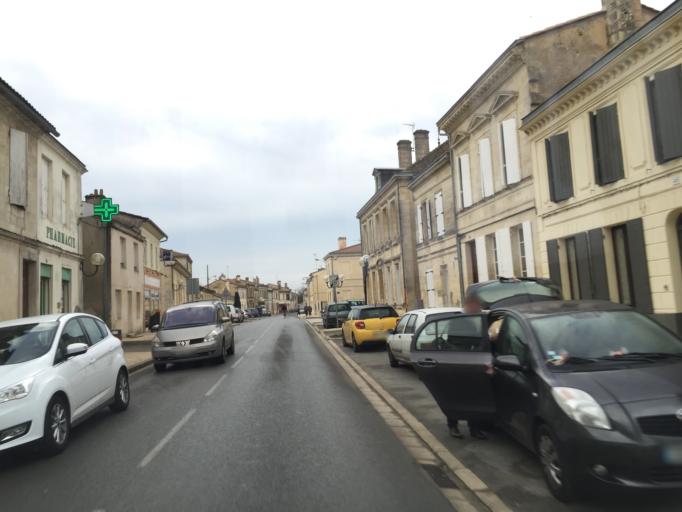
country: FR
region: Aquitaine
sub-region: Departement de la Gironde
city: Lamarque
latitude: 45.0960
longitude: -0.7179
